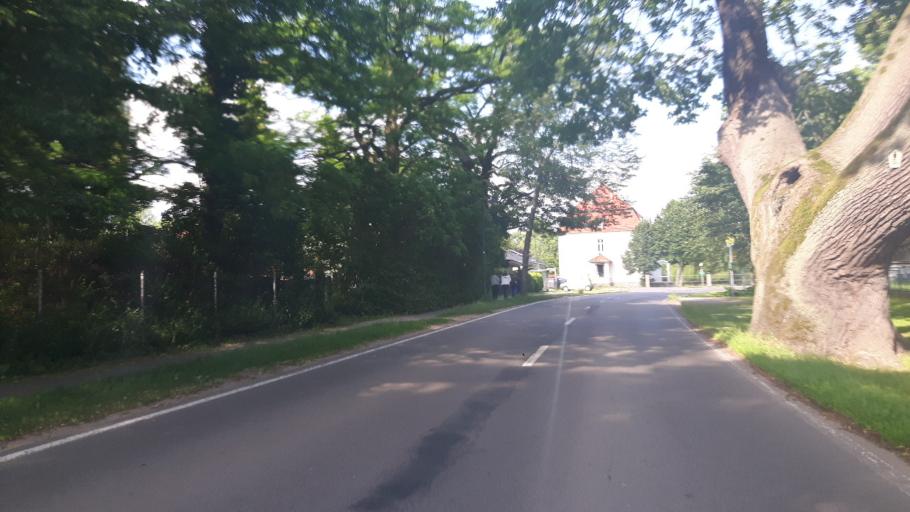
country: DE
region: Brandenburg
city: Melchow
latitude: 52.7431
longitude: 13.7216
